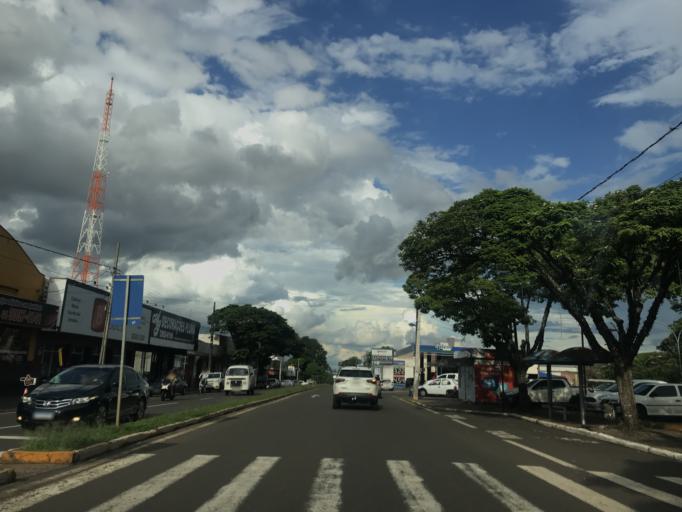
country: BR
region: Parana
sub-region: Maringa
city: Maringa
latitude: -23.4264
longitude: -51.9639
